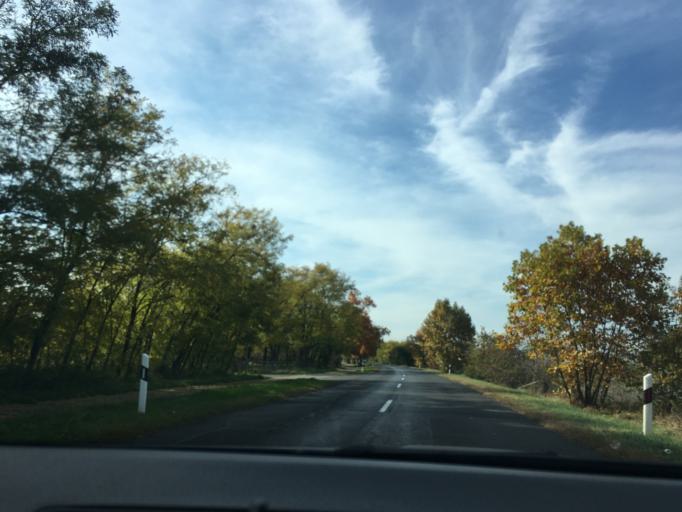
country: HU
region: Hajdu-Bihar
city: Vamospercs
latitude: 47.5269
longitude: 21.9277
